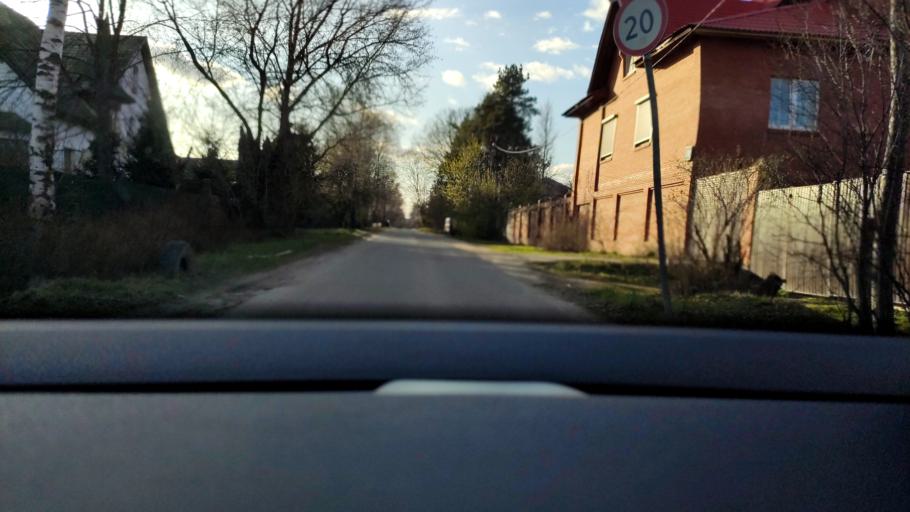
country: RU
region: Moskovskaya
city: Reutov
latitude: 55.7709
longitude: 37.8941
